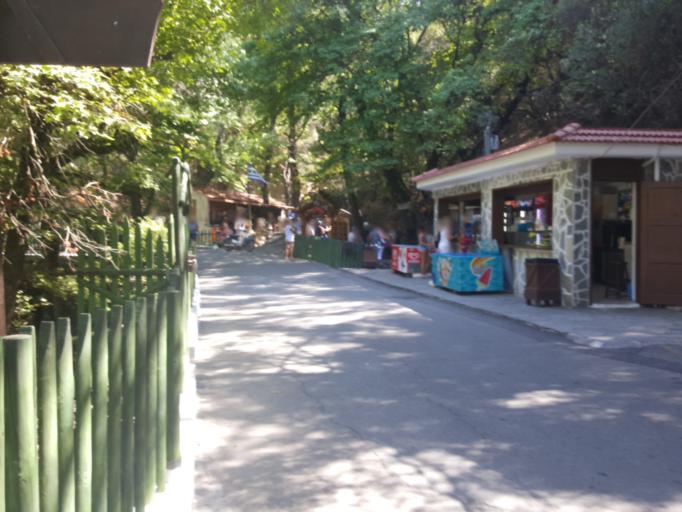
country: GR
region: South Aegean
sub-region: Nomos Dodekanisou
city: Kremasti
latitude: 36.3371
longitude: 28.0616
